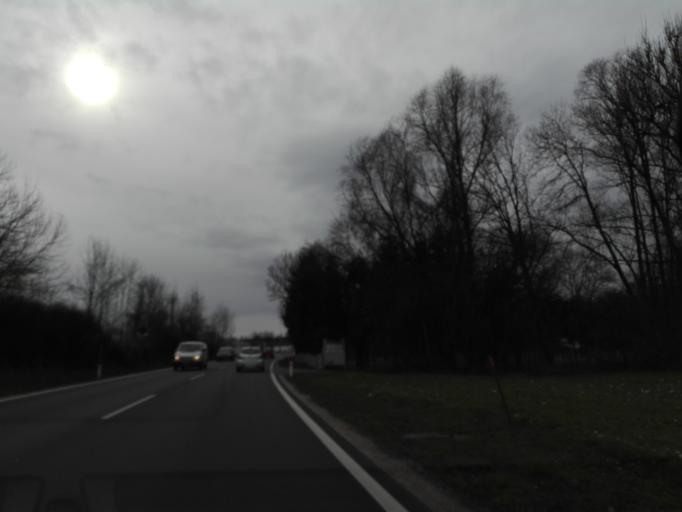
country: AT
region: Upper Austria
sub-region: Politischer Bezirk Linz-Land
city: Traun
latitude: 48.2126
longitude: 14.2549
